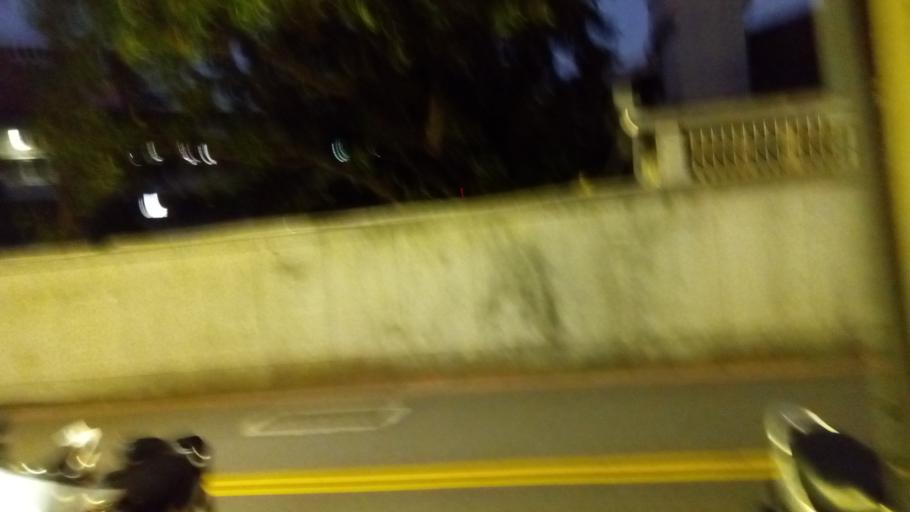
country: TW
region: Taipei
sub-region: Taipei
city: Banqiao
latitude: 25.0336
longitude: 121.4319
